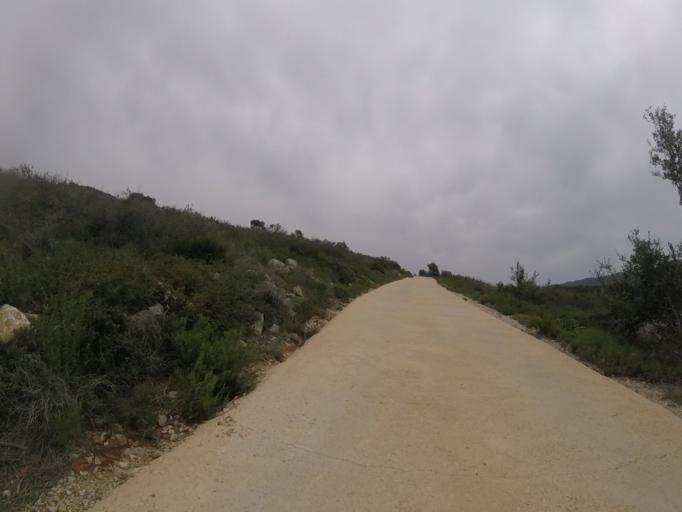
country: ES
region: Valencia
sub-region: Provincia de Castello
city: Alcala de Xivert
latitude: 40.2948
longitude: 0.2552
